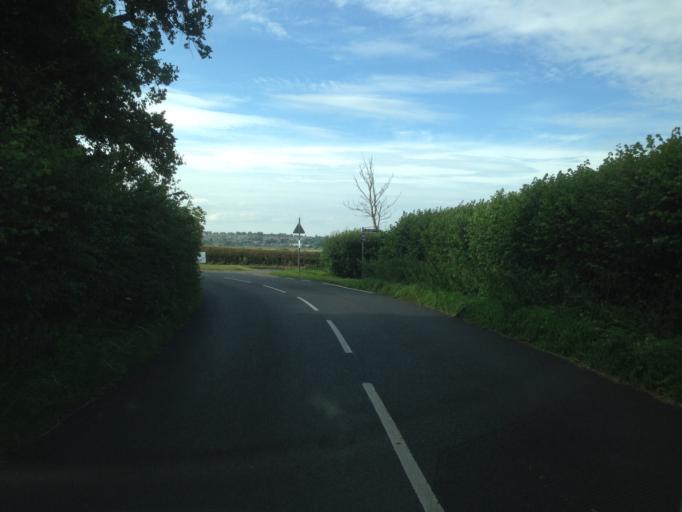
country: GB
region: England
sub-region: Isle of Wight
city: Bembridge
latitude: 50.6750
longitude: -1.1044
